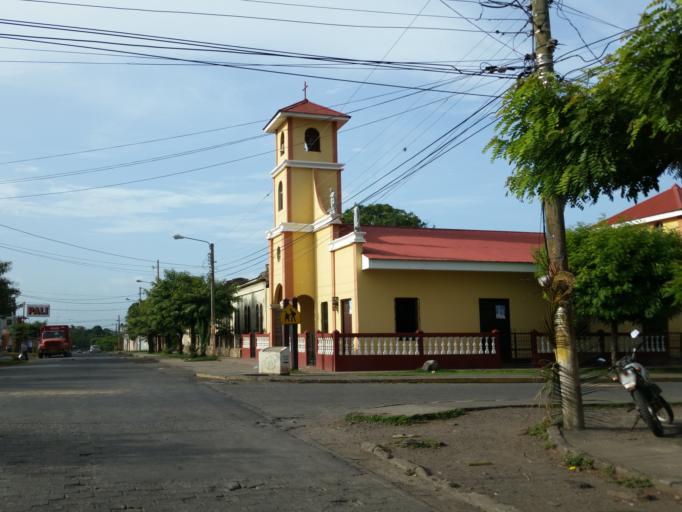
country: NI
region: Granada
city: Granada
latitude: 11.9368
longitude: -85.9532
